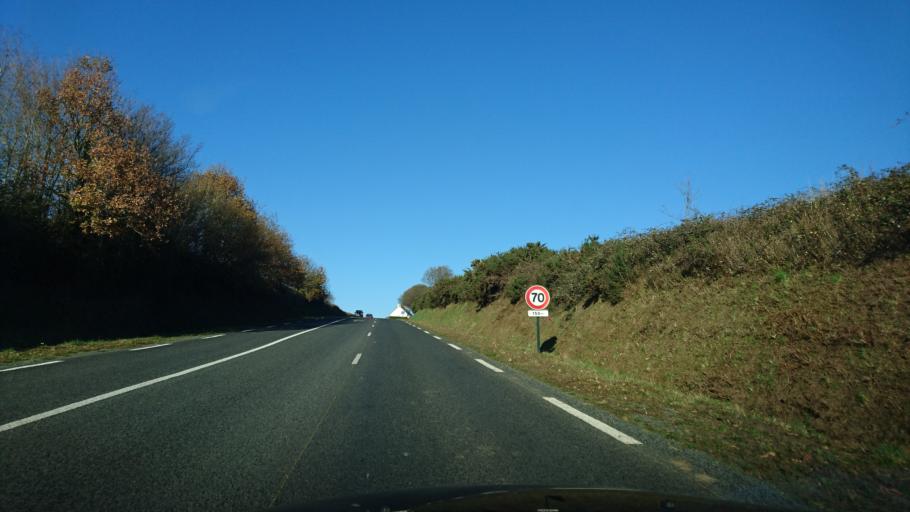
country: FR
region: Brittany
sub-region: Departement des Cotes-d'Armor
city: Pledran
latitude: 48.4706
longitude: -2.7516
